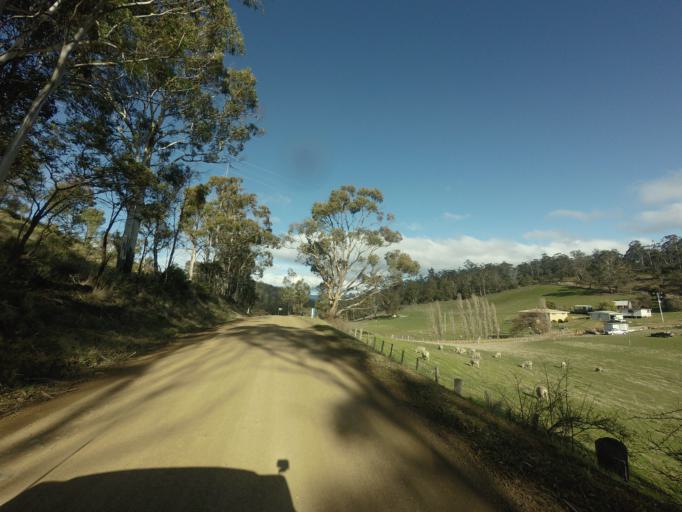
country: AU
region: Tasmania
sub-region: Derwent Valley
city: New Norfolk
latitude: -42.7066
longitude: 147.0193
